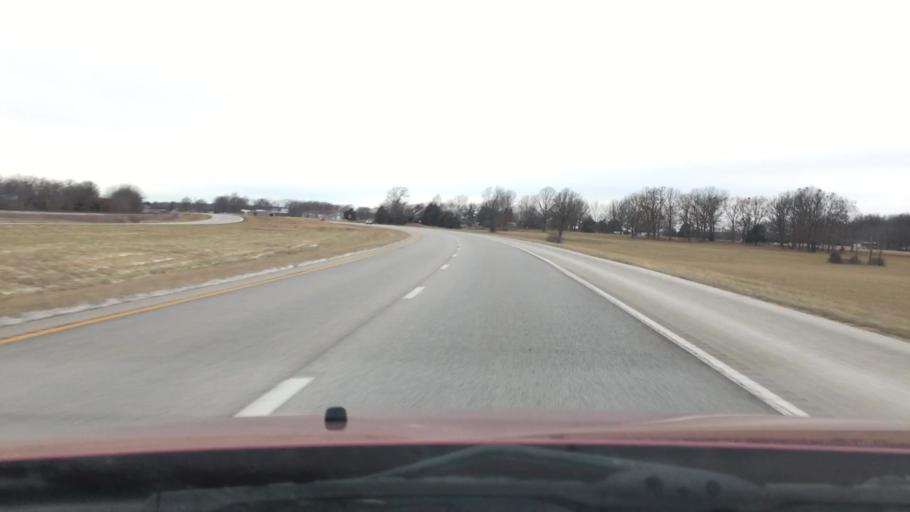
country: US
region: Missouri
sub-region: Webster County
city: Seymour
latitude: 37.1681
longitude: -92.8056
